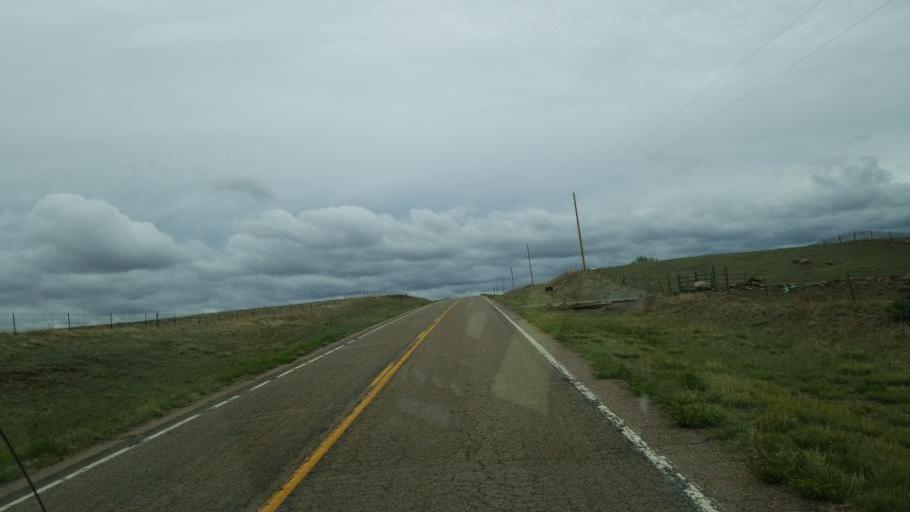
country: US
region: Colorado
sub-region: Lincoln County
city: Limon
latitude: 38.8381
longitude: -103.8561
